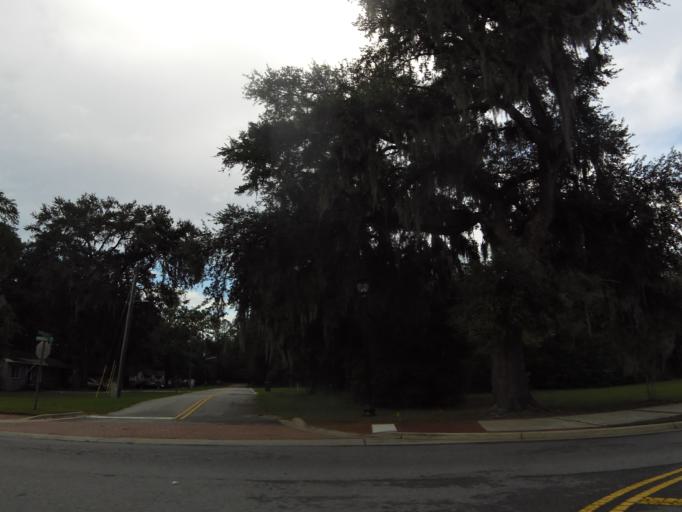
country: US
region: Georgia
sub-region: Liberty County
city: Hinesville
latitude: 31.8502
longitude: -81.5970
